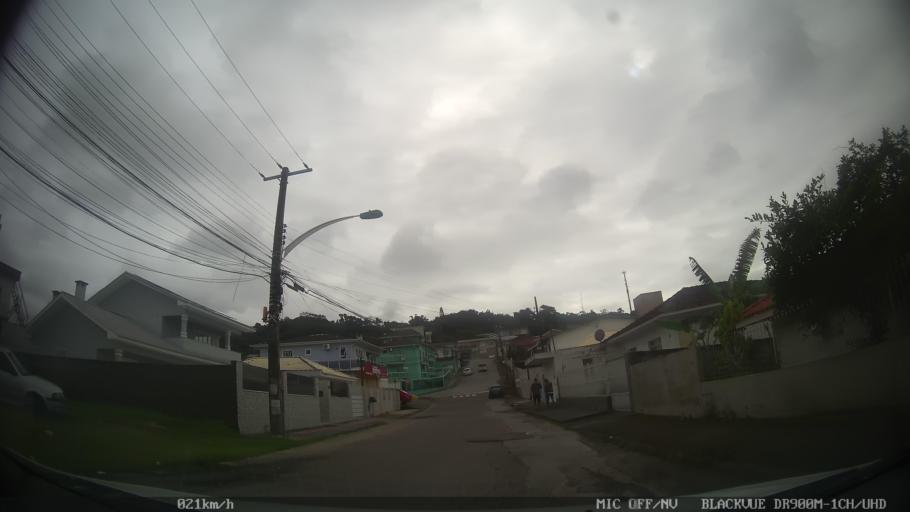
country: BR
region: Santa Catarina
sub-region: Biguacu
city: Biguacu
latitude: -27.5225
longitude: -48.6397
